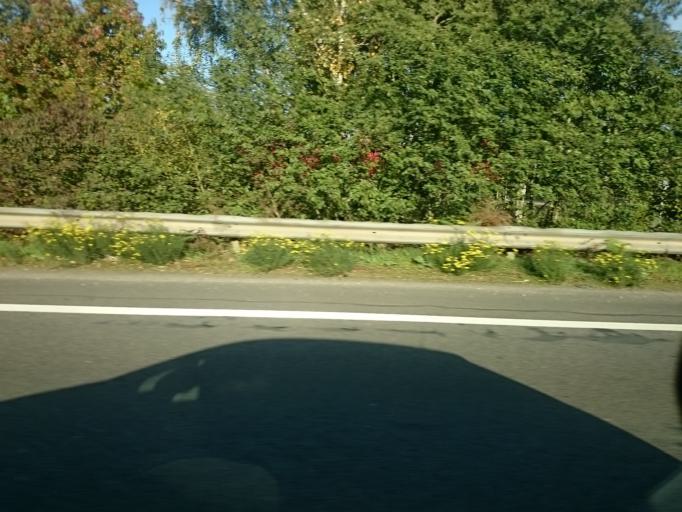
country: FR
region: Pays de la Loire
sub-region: Departement de la Loire-Atlantique
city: Orvault
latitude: 47.2719
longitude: -1.5919
